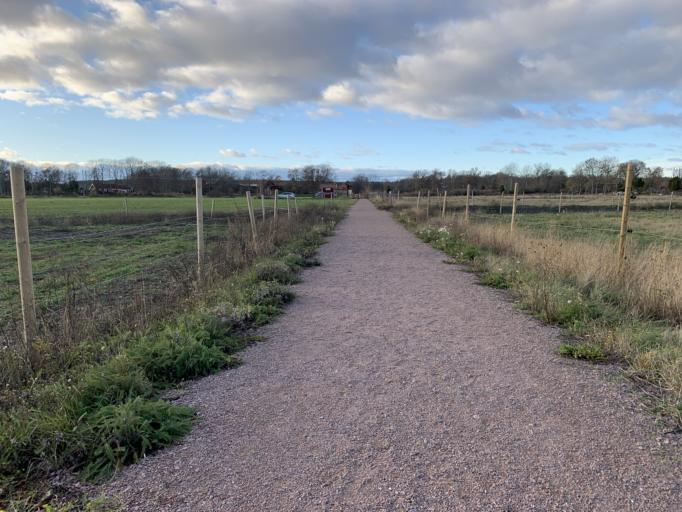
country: SE
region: Soedermanland
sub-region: Eskilstuna Kommun
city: Torshalla
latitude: 59.5236
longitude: 16.4473
